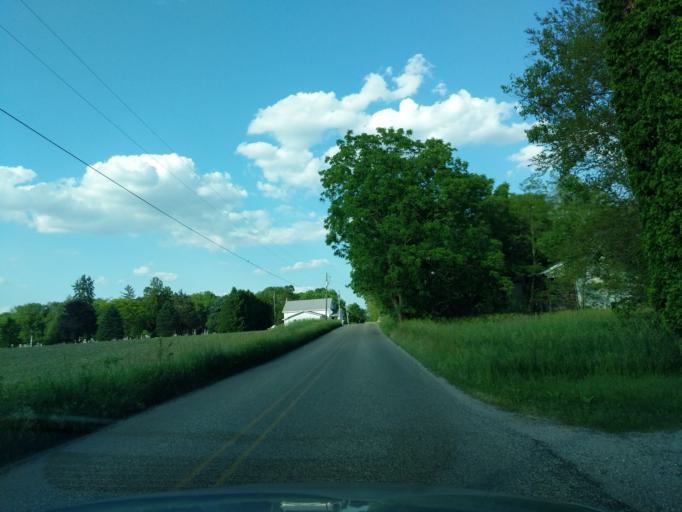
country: US
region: Indiana
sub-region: Kosciusko County
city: North Webster
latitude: 41.3061
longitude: -85.6381
